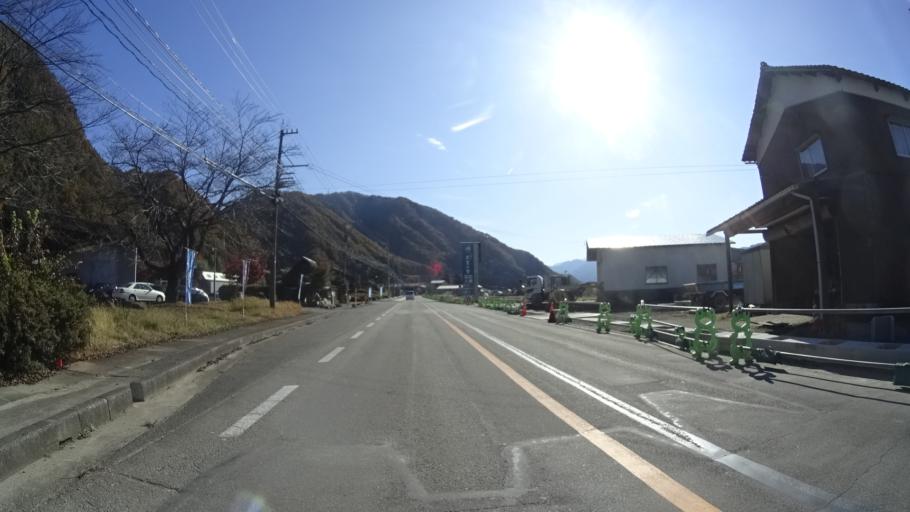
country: JP
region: Ishikawa
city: Tsurugi-asahimachi
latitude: 36.3574
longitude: 136.6209
